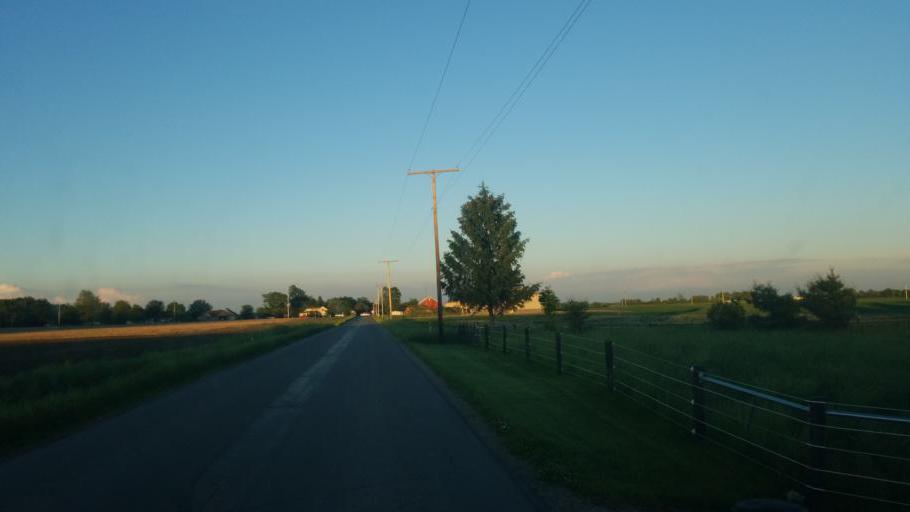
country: US
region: Indiana
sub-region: Elkhart County
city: Nappanee
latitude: 41.4266
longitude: -86.0065
